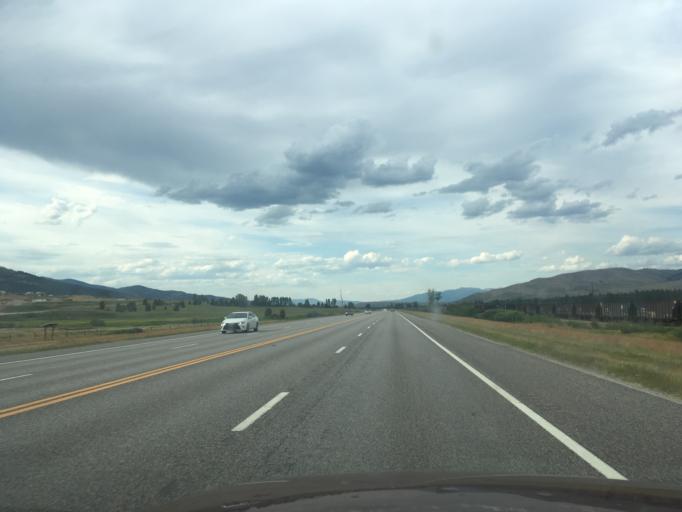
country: US
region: Montana
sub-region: Missoula County
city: Lolo
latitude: 46.6877
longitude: -114.0741
